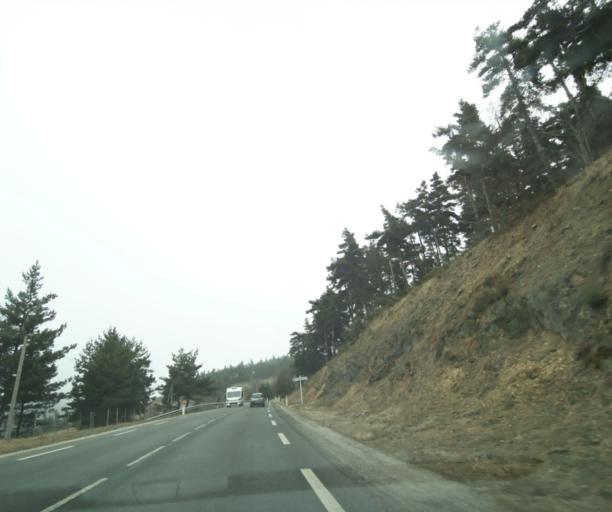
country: FR
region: Languedoc-Roussillon
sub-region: Departement de la Lozere
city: Langogne
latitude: 44.6701
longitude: 3.7636
